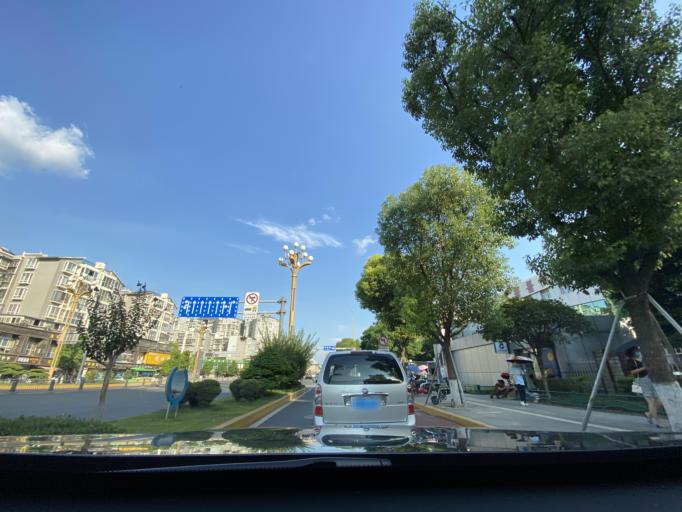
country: CN
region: Sichuan
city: Jiancheng
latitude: 30.4115
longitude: 104.5370
